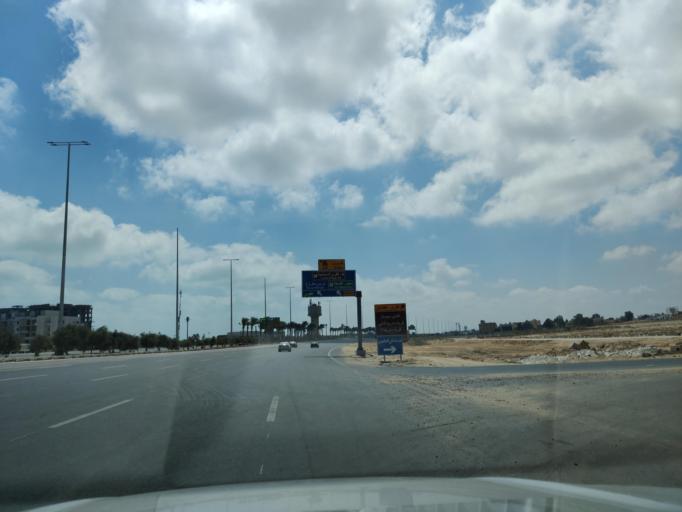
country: EG
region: Muhafazat Matruh
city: Al `Alamayn
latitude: 30.8449
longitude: 28.9411
